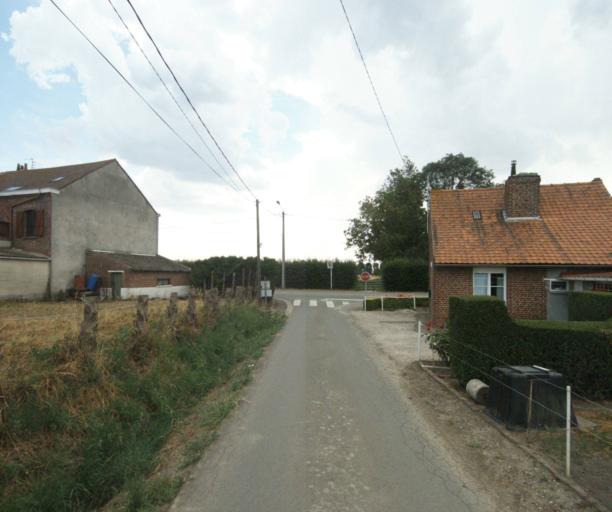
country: FR
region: Nord-Pas-de-Calais
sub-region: Departement du Nord
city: Deulemont
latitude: 50.7284
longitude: 2.9701
